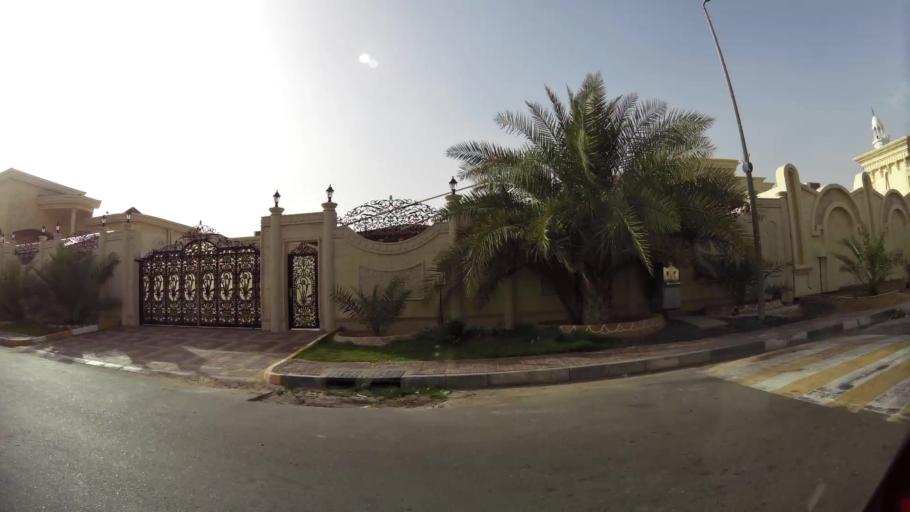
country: AE
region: Abu Dhabi
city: Al Ain
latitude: 24.2185
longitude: 55.6489
